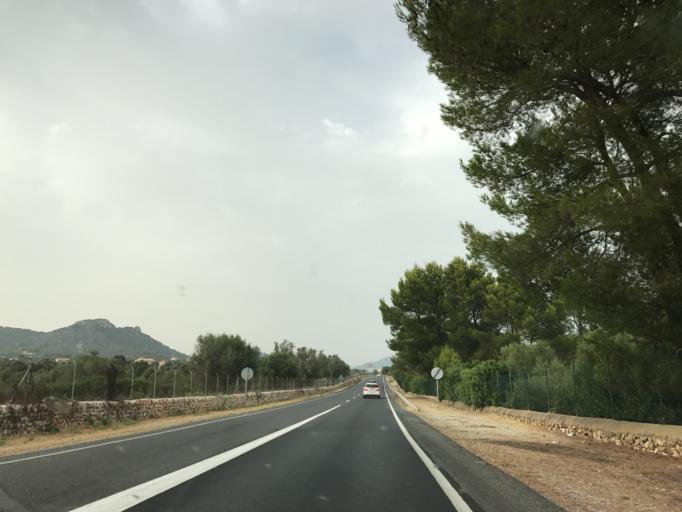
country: ES
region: Balearic Islands
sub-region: Illes Balears
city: Son Servera
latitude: 39.5852
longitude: 3.3649
